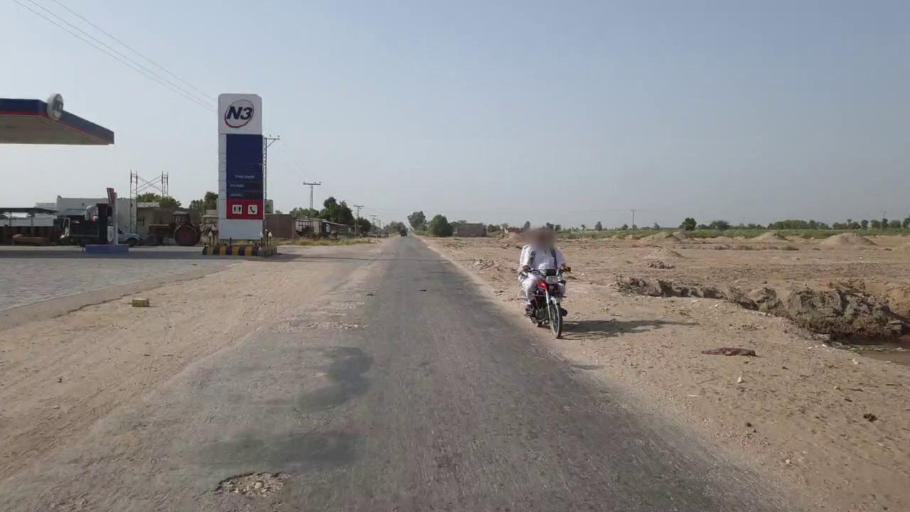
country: PK
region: Sindh
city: Sanghar
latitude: 26.2857
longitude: 68.9308
